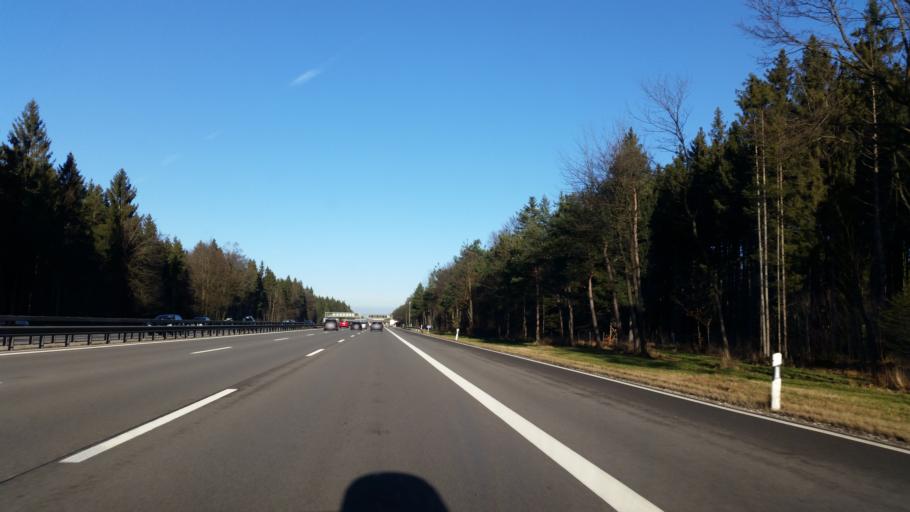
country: DE
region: Bavaria
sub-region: Upper Bavaria
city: Otterfing
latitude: 47.9321
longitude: 11.7076
